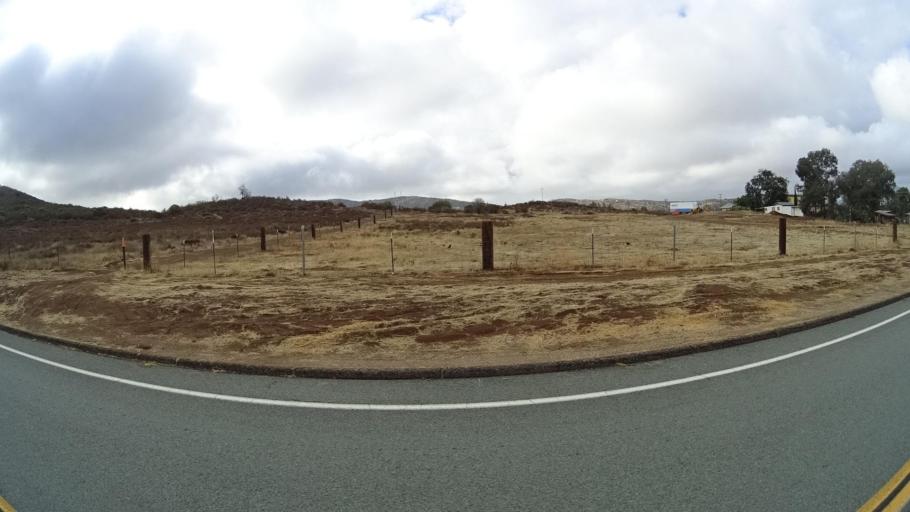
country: MX
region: Baja California
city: Tecate
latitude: 32.6152
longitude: -116.6113
